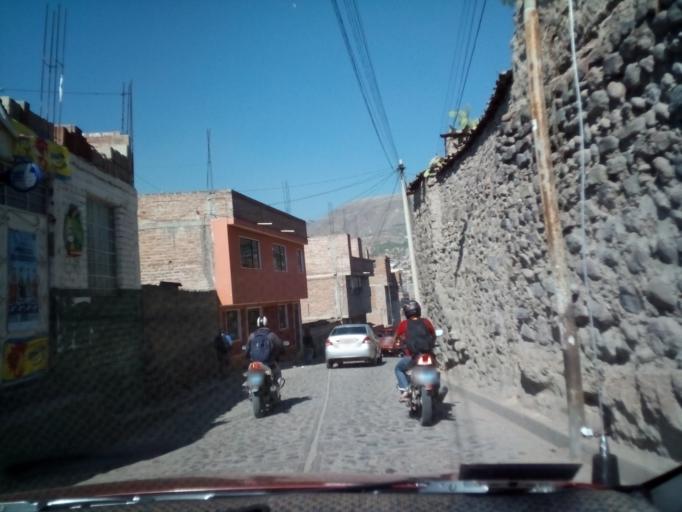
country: PE
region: Ayacucho
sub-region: Provincia de Huamanga
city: Ayacucho
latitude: -13.1613
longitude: -74.2206
